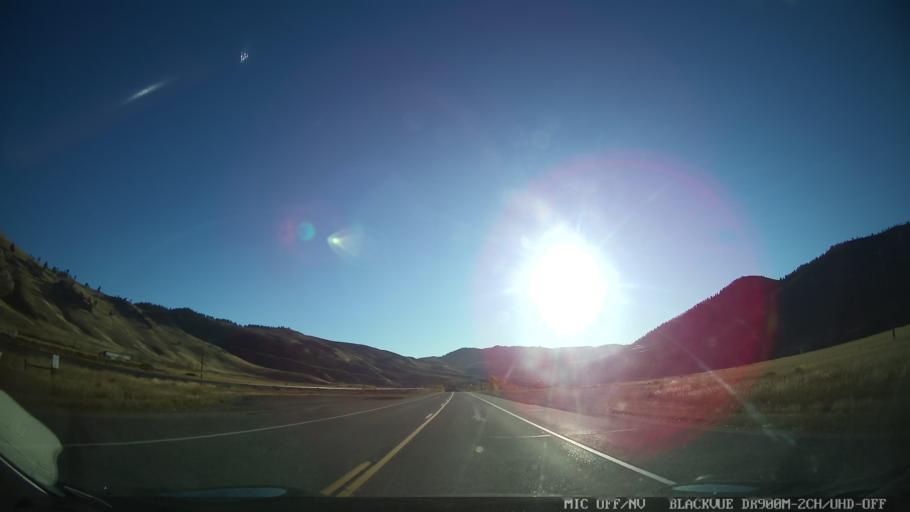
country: US
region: Colorado
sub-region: Grand County
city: Hot Sulphur Springs
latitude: 40.0508
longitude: -106.1433
